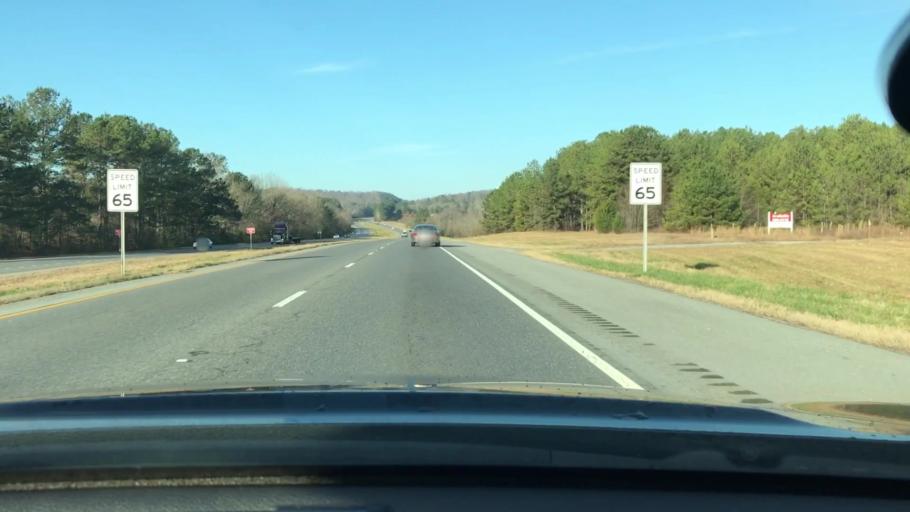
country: US
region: Alabama
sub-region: Shelby County
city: Harpersville
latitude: 33.3495
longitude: -86.4619
